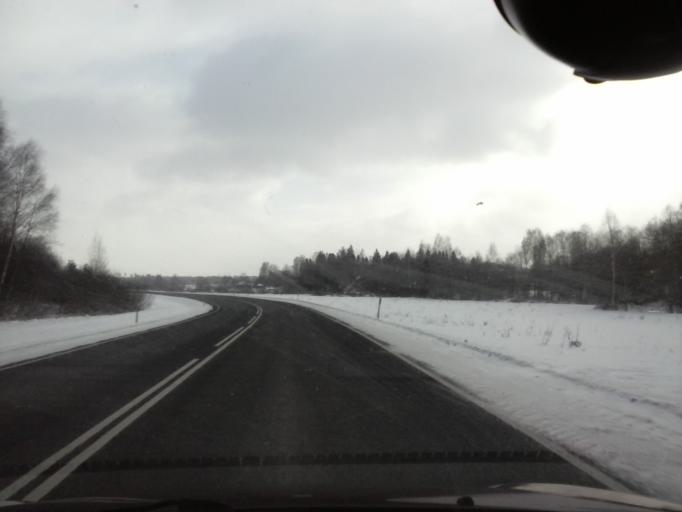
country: EE
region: Viljandimaa
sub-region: Viljandi linn
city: Viljandi
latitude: 58.3451
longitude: 25.4653
